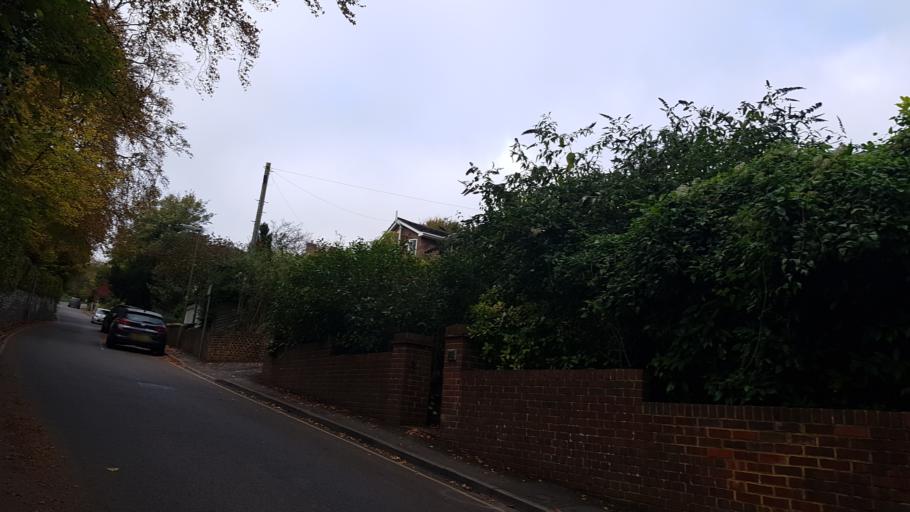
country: GB
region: England
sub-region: Surrey
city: Guildford
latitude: 51.2322
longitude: -0.5818
